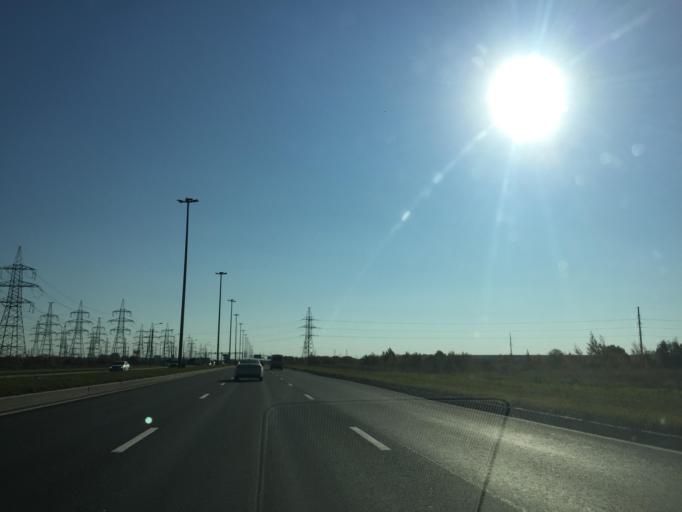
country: RU
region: St.-Petersburg
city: Petro-Slavyanka
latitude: 59.7561
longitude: 30.5187
